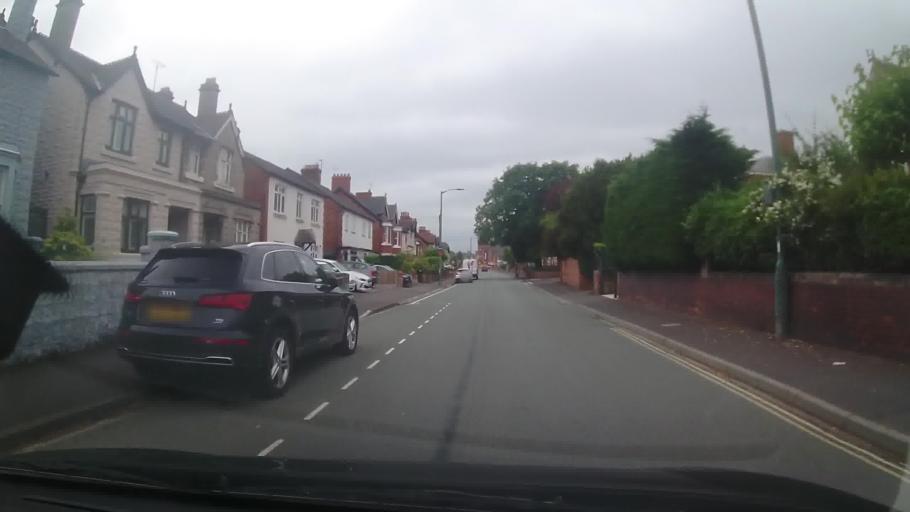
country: GB
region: England
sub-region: Shropshire
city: Shrewsbury
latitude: 52.7103
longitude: -2.7683
